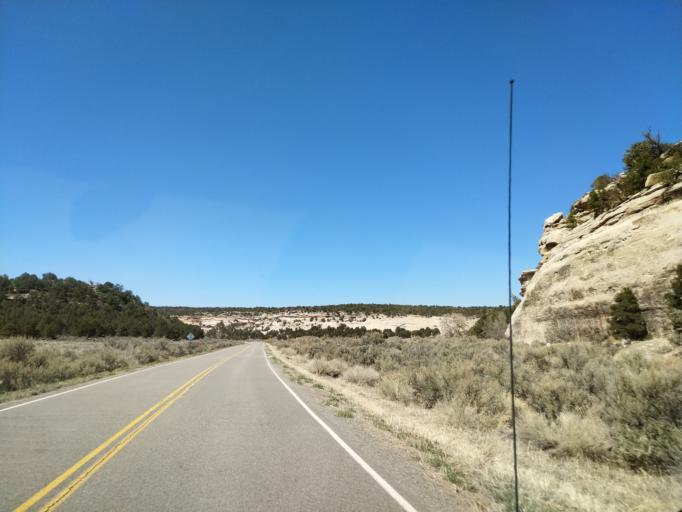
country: US
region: Colorado
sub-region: Mesa County
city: Redlands
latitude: 38.9885
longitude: -108.7808
